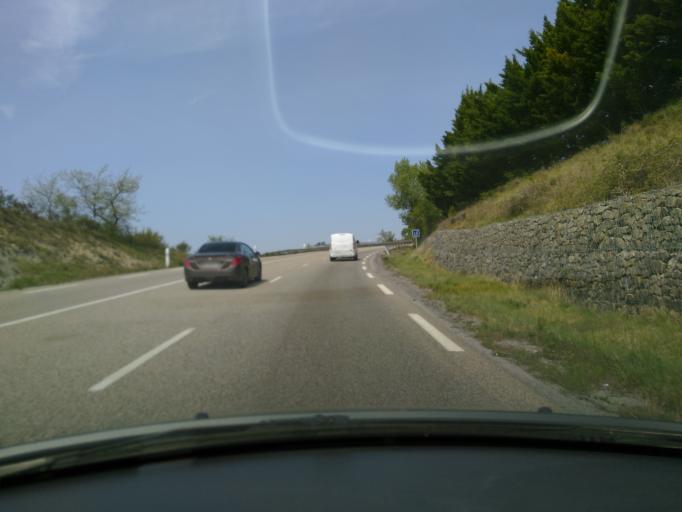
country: FR
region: Rhone-Alpes
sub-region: Departement de l'Ardeche
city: Villeneuve-de-Berg
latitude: 44.5679
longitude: 4.5007
